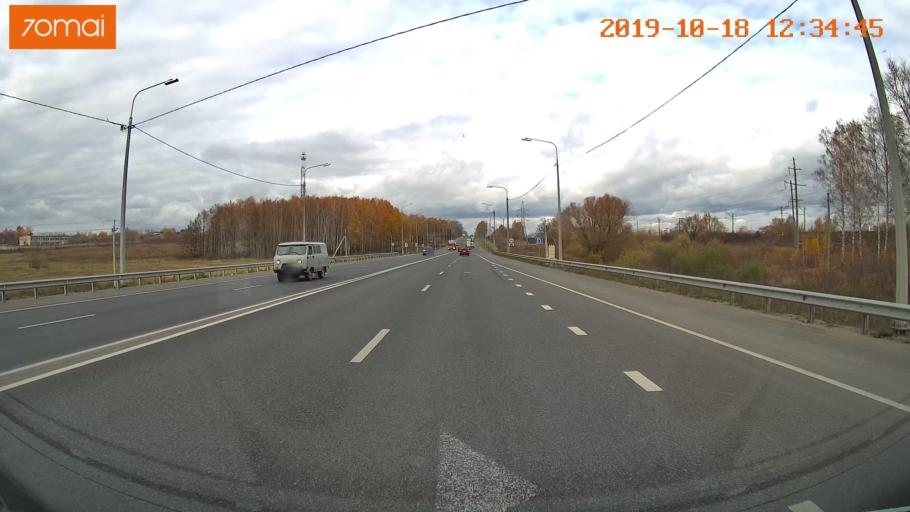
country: RU
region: Rjazan
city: Ryazan'
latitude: 54.6174
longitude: 39.6369
